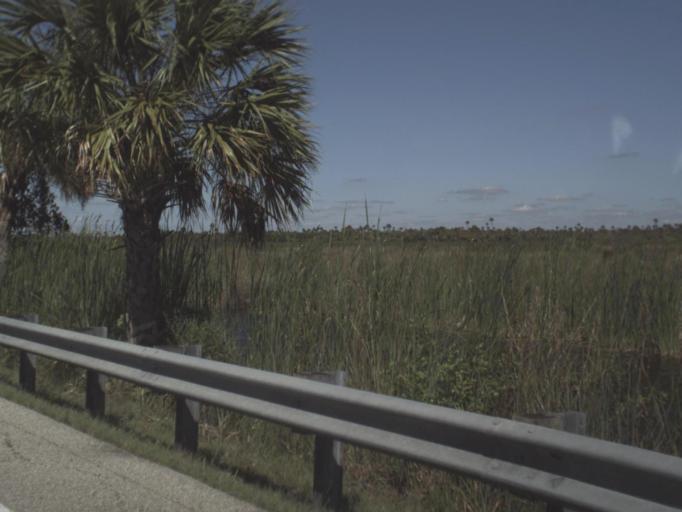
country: US
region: Florida
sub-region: Collier County
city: Marco
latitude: 25.9271
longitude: -81.4290
